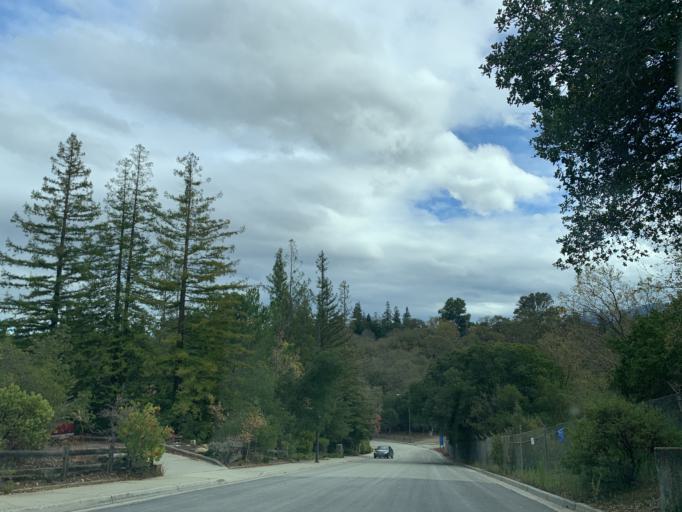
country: US
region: California
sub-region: Santa Clara County
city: Monte Sereno
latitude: 37.2576
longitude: -121.9819
